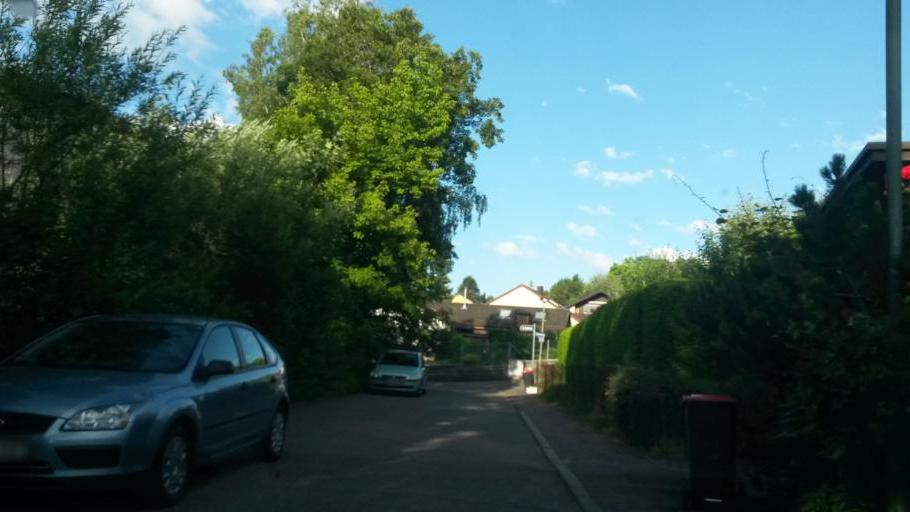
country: DE
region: Baden-Wuerttemberg
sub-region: Karlsruhe Region
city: Unterreichenbach
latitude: 48.8567
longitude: 8.7337
